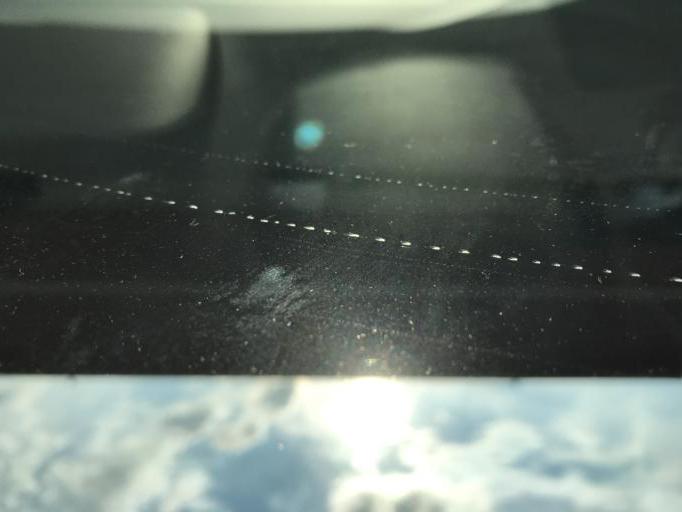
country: US
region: Michigan
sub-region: Oakland County
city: Novi
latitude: 42.4778
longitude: -83.4680
